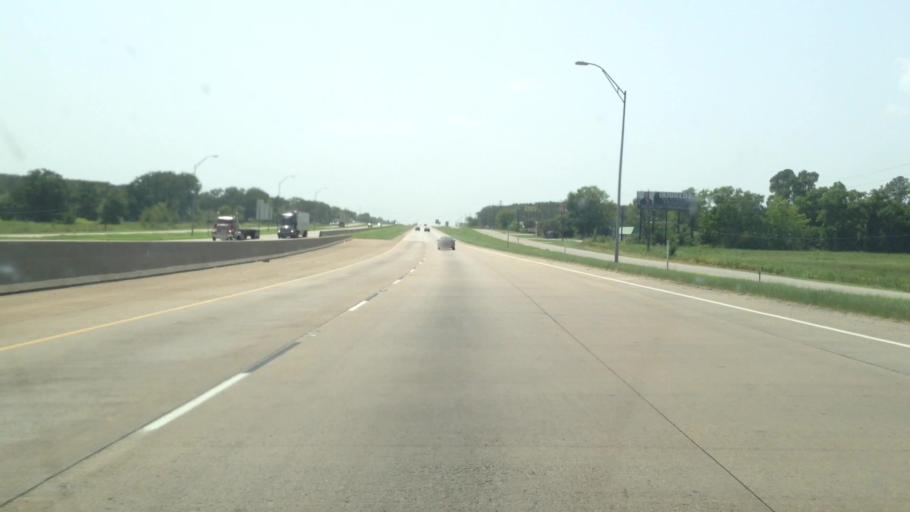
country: US
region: Texas
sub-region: Hopkins County
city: Sulphur Springs
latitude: 33.1211
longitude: -95.6396
